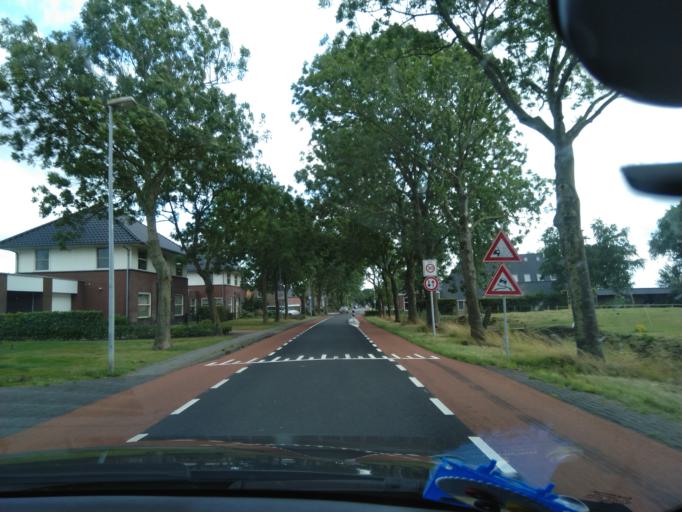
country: NL
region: Groningen
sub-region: Gemeente Zuidhorn
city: Aduard
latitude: 53.2297
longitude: 6.5001
